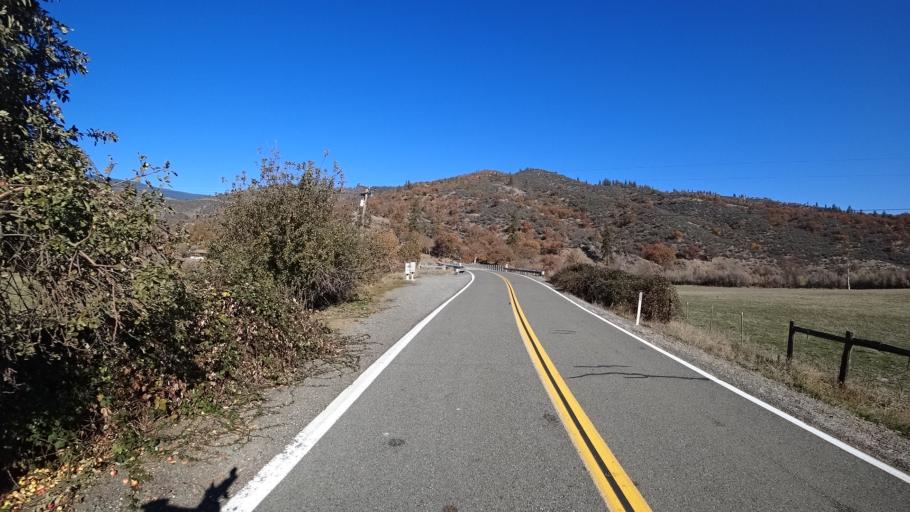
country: US
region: California
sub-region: Siskiyou County
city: Yreka
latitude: 41.8363
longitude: -122.8649
